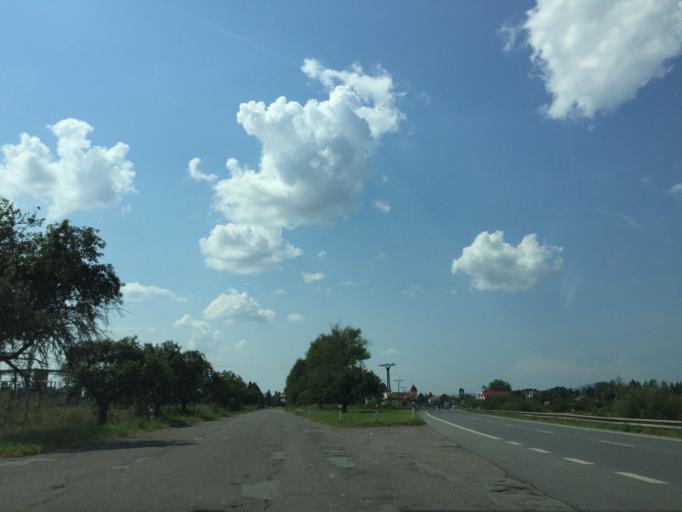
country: SK
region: Kosicky
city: Sobrance
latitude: 48.7415
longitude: 22.1917
